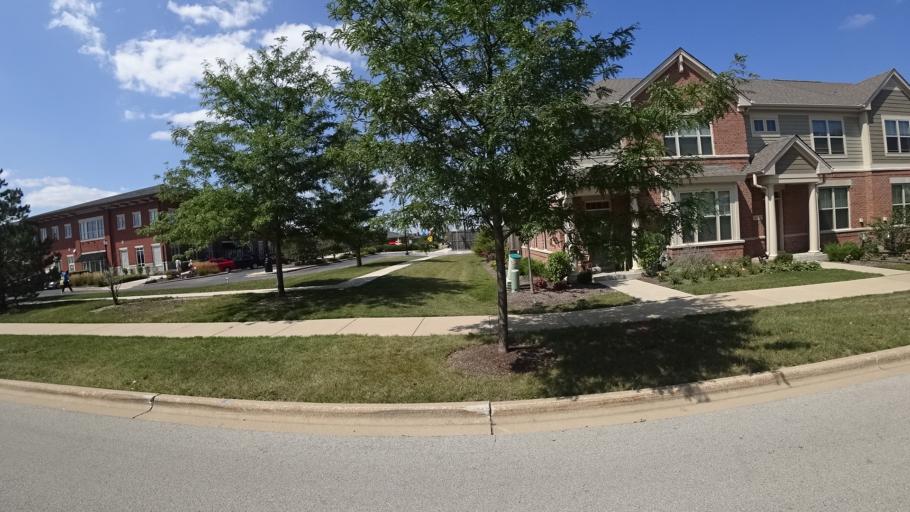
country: US
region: Illinois
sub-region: Cook County
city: Orland Park
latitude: 41.6329
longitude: -87.8504
